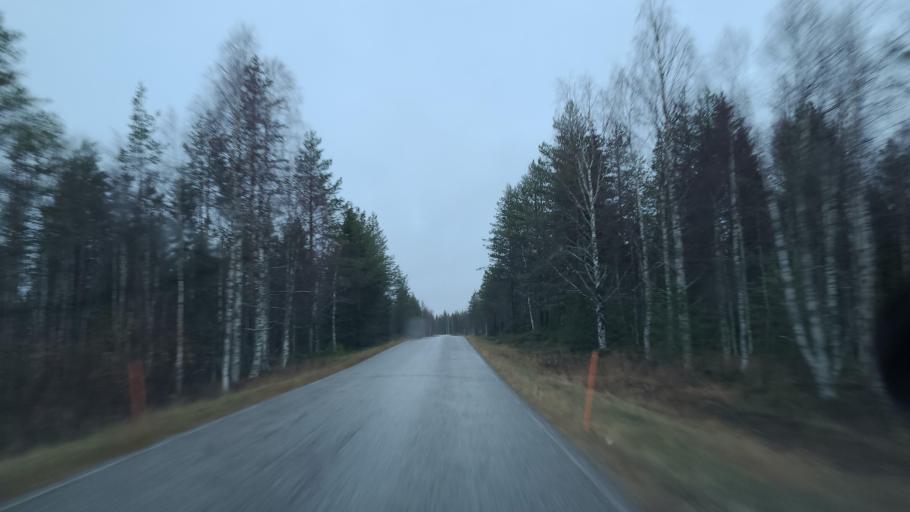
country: FI
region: Lapland
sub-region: Kemi-Tornio
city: Simo
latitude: 65.9219
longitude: 25.2006
